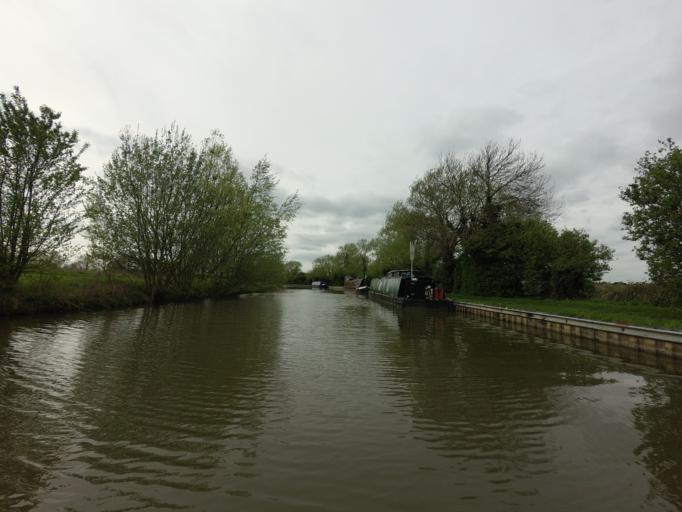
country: GB
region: England
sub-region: Milton Keynes
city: Bradwell
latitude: 52.0740
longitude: -0.7791
